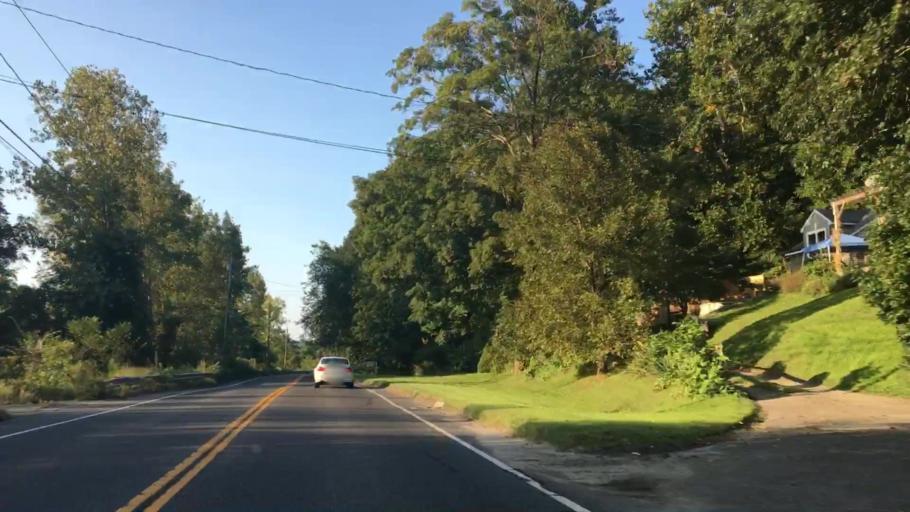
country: US
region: Connecticut
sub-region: Litchfield County
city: New Milford
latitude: 41.5556
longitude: -73.4056
